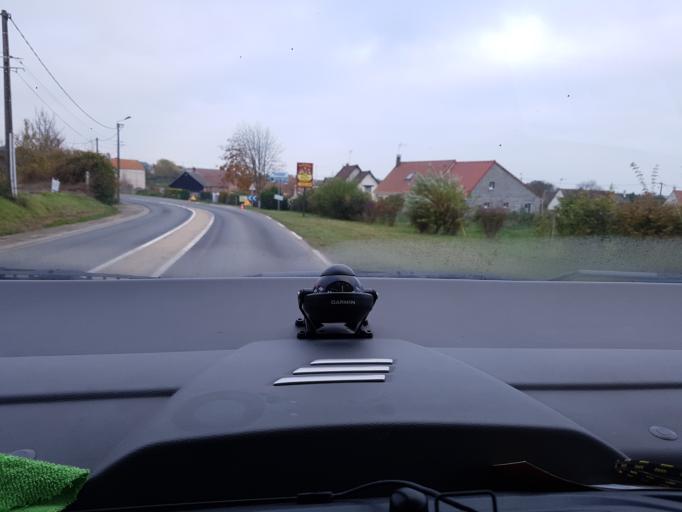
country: FR
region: Picardie
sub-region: Departement de la Somme
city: Ault
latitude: 50.1255
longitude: 1.4889
